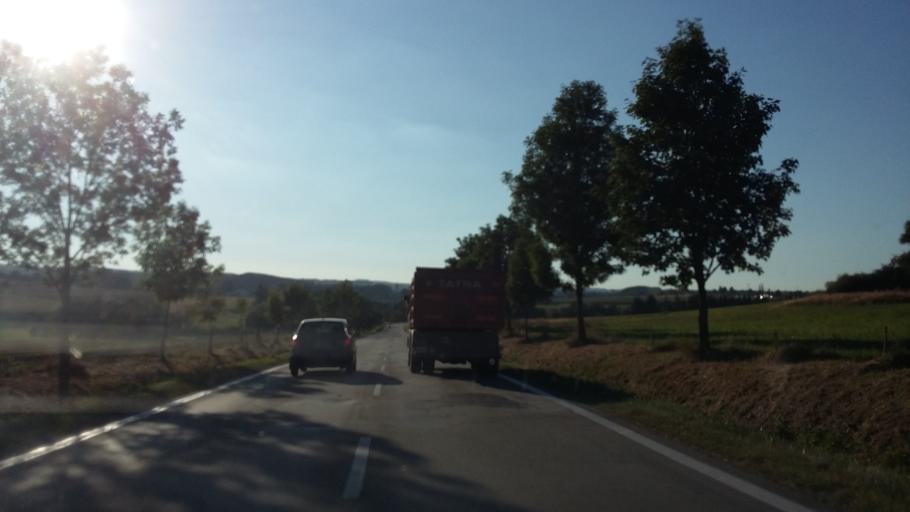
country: CZ
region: Vysocina
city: Merin
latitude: 49.3833
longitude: 15.9167
